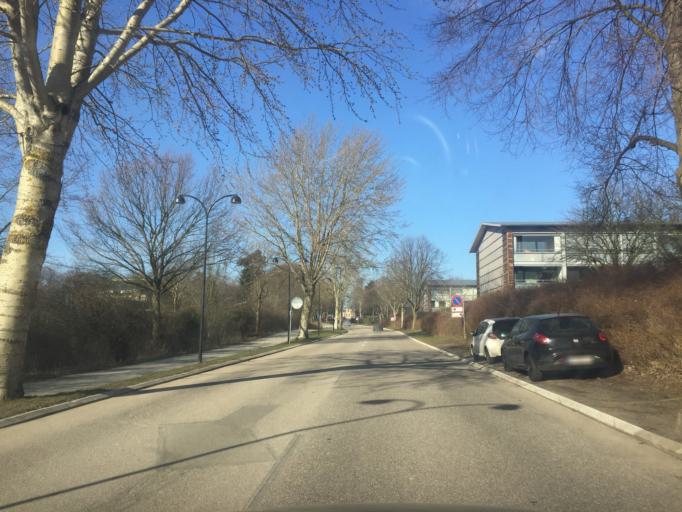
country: DK
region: Capital Region
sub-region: Rudersdal Kommune
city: Trorod
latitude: 55.8554
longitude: 12.5589
